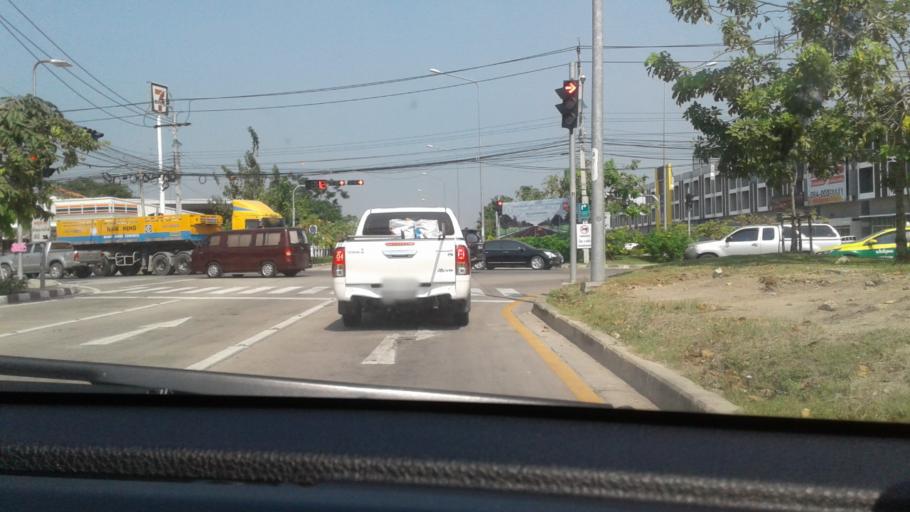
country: TH
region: Bangkok
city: Thawi Watthana
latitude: 13.7986
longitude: 100.3636
